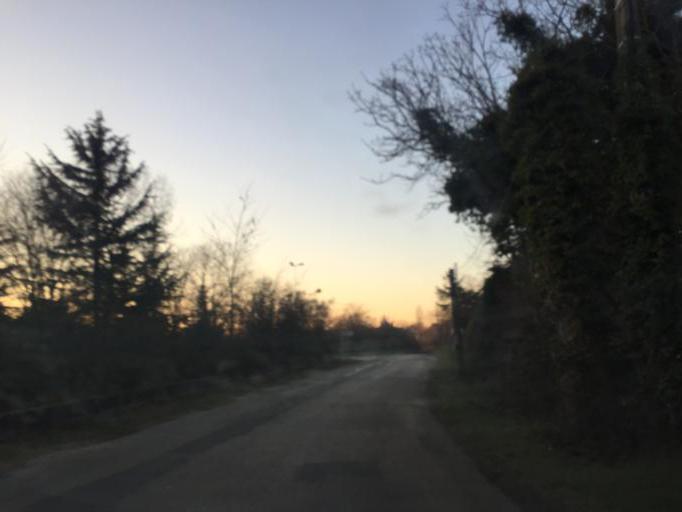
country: FR
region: Rhone-Alpes
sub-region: Departement de l'Ain
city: Saint-Maurice-de-Gourdans
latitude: 45.8479
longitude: 5.1637
